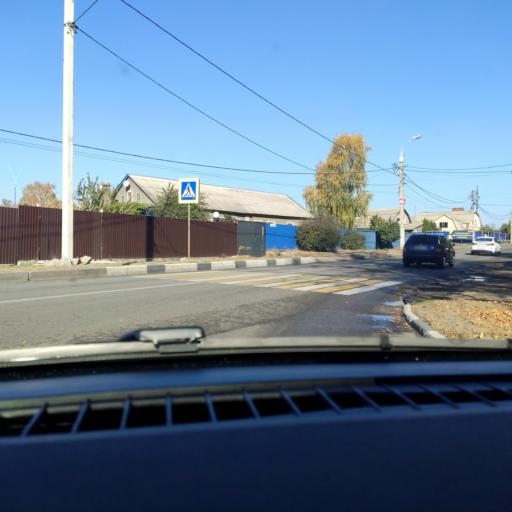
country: RU
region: Voronezj
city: Pridonskoy
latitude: 51.6869
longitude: 39.0790
